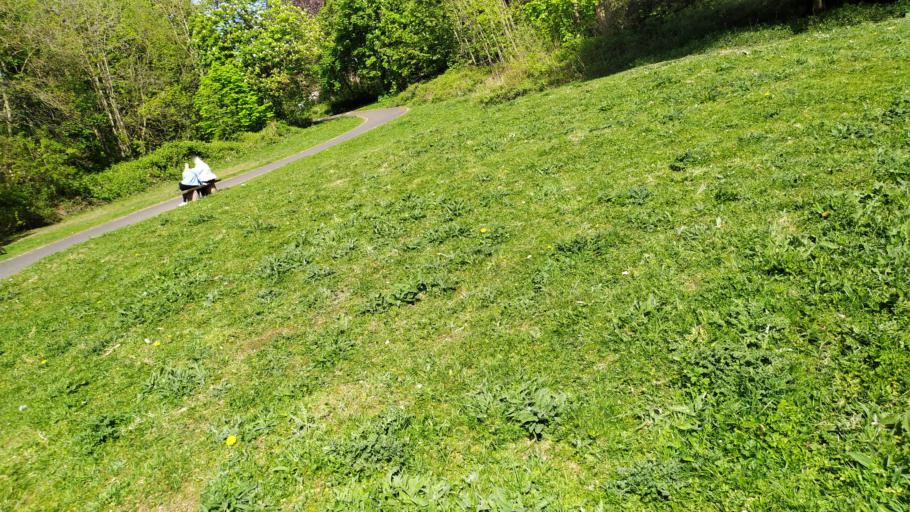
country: GB
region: England
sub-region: City and Borough of Leeds
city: Shadwell
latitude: 53.8065
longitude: -1.4814
